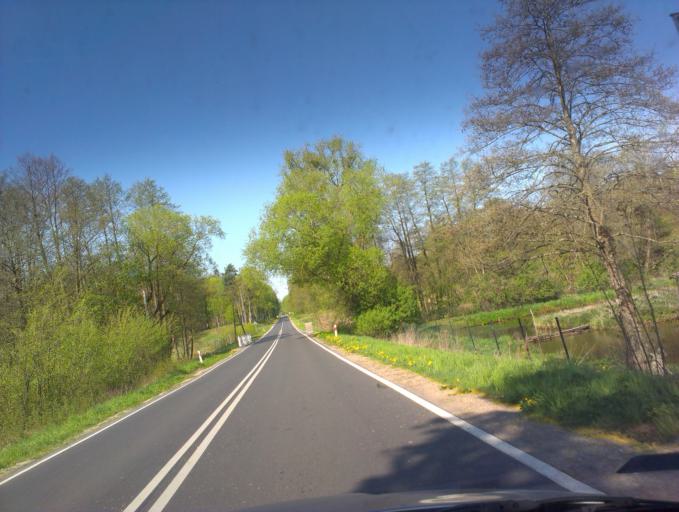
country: PL
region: West Pomeranian Voivodeship
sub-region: Powiat swidwinski
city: Polczyn-Zdroj
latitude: 53.7704
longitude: 16.1458
